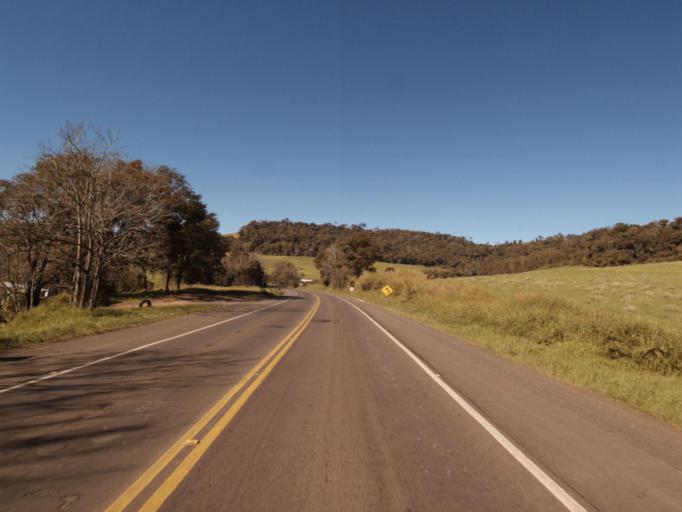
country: BR
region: Rio Grande do Sul
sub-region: Frederico Westphalen
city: Frederico Westphalen
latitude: -26.8001
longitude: -53.3201
